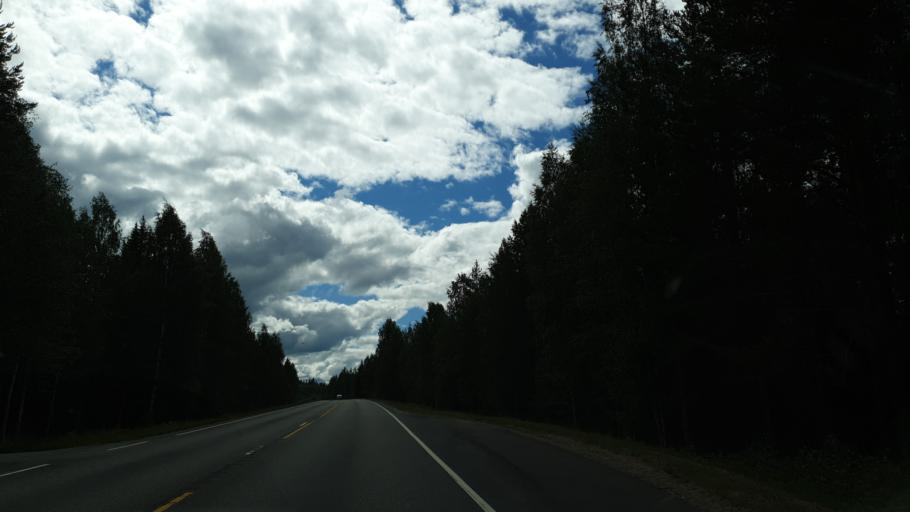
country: FI
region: North Karelia
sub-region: Pielisen Karjala
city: Valtimo
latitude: 63.5112
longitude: 28.8546
